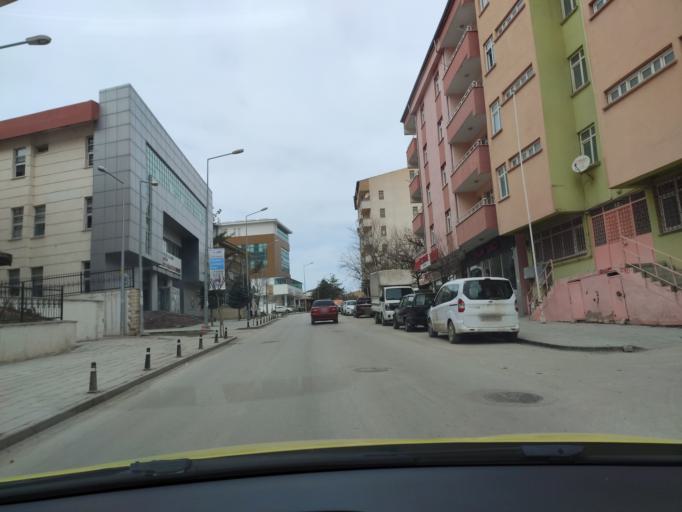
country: TR
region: Bayburt
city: Bayburt
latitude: 40.2538
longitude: 40.2241
